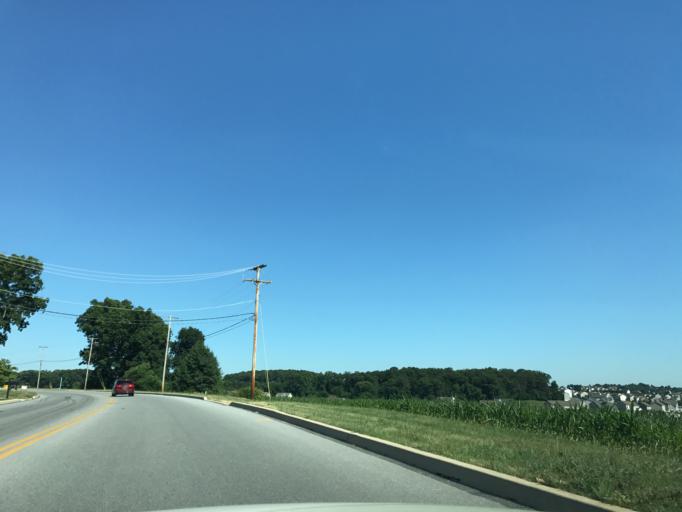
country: US
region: Pennsylvania
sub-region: York County
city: Parkville
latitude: 39.7680
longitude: -76.9761
